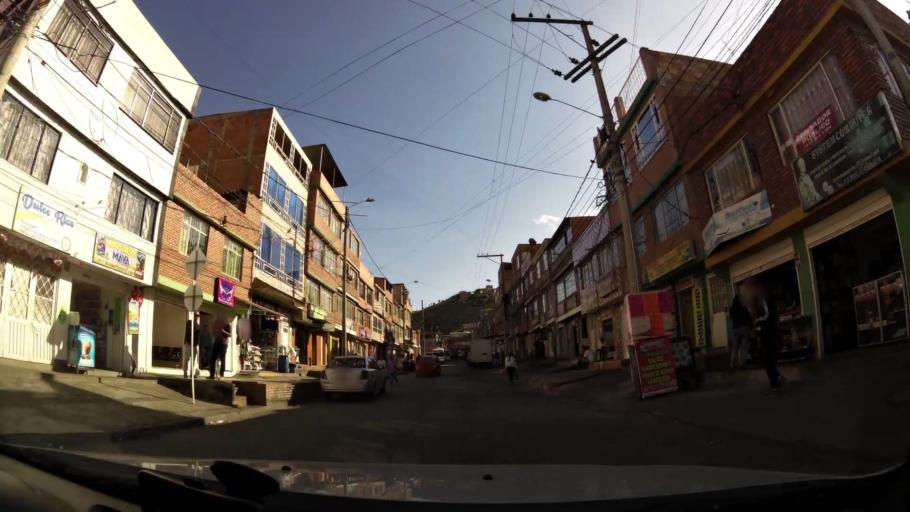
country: CO
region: Cundinamarca
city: Soacha
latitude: 4.5683
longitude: -74.1499
